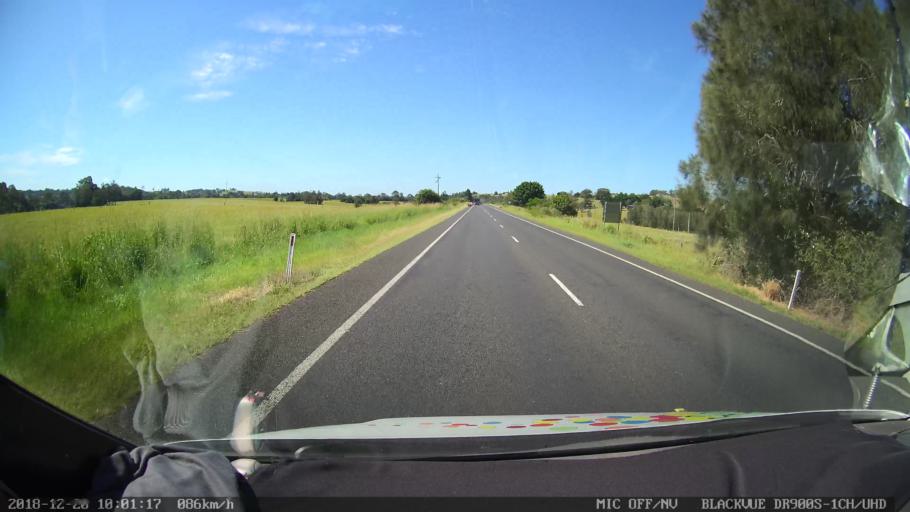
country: AU
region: New South Wales
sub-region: Lismore Municipality
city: Lismore
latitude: -28.8424
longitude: 153.2629
